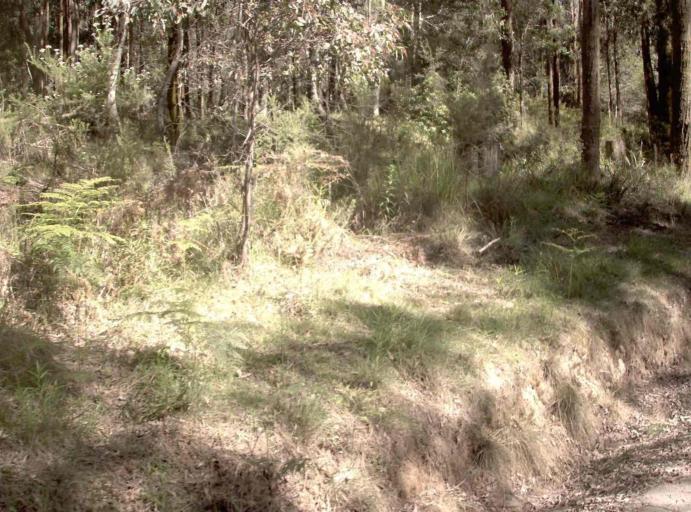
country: AU
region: New South Wales
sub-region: Bombala
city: Bombala
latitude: -37.2054
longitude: 148.7313
